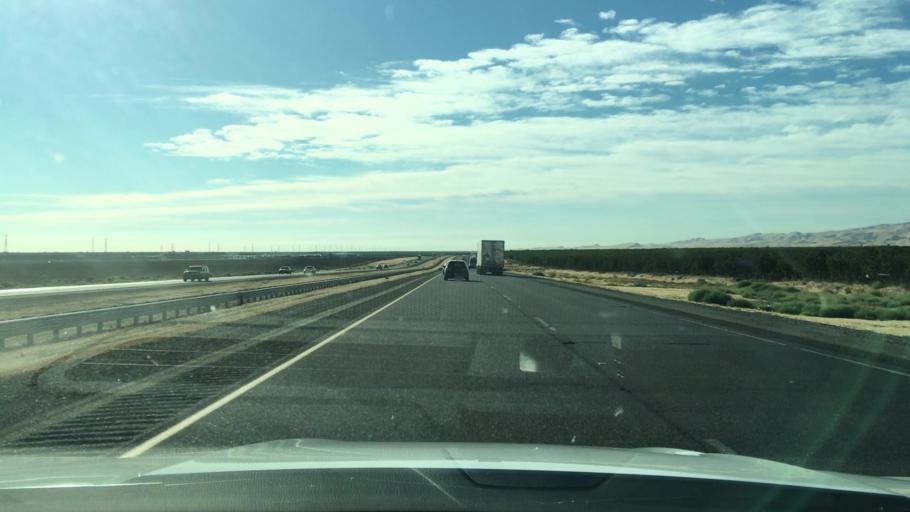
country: US
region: California
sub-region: Fresno County
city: San Joaquin
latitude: 36.4580
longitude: -120.4147
